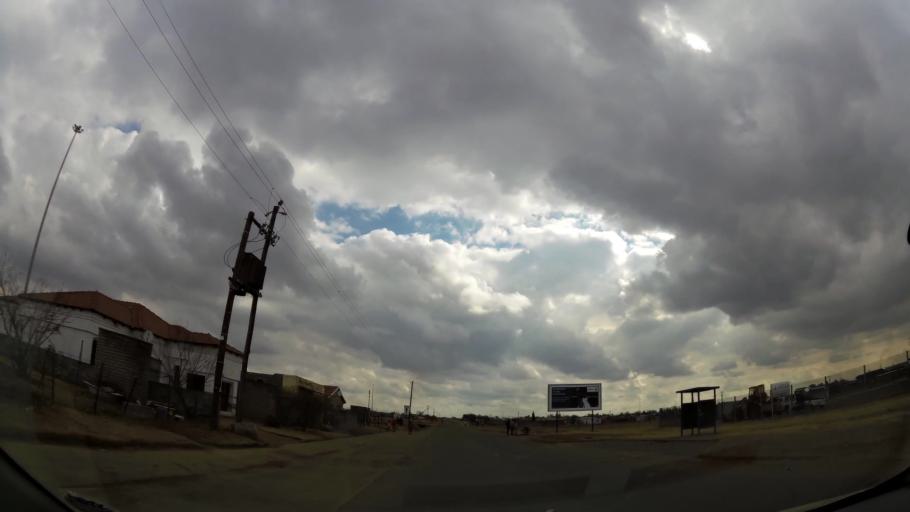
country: ZA
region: Orange Free State
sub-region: Fezile Dabi District Municipality
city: Sasolburg
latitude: -26.8552
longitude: 27.8798
